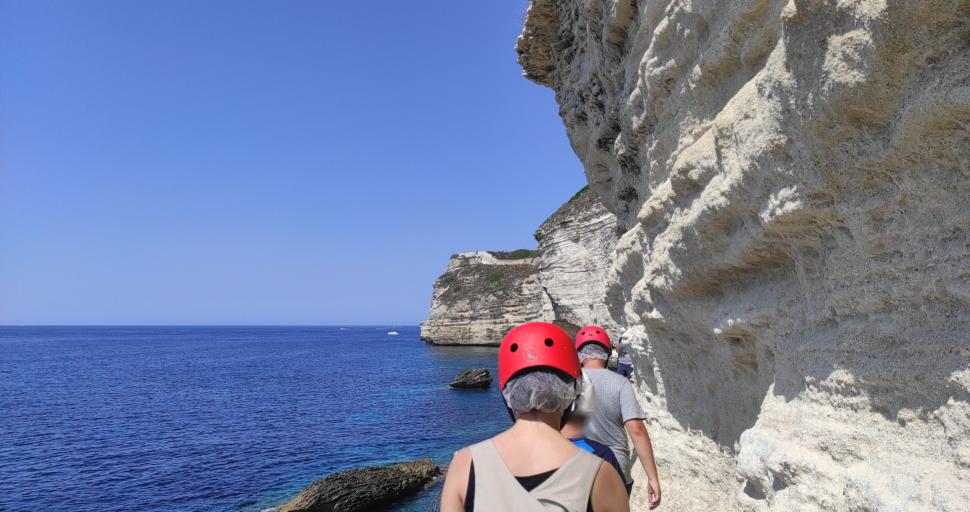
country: FR
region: Corsica
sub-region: Departement de la Corse-du-Sud
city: Bonifacio
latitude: 41.3862
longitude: 9.1547
